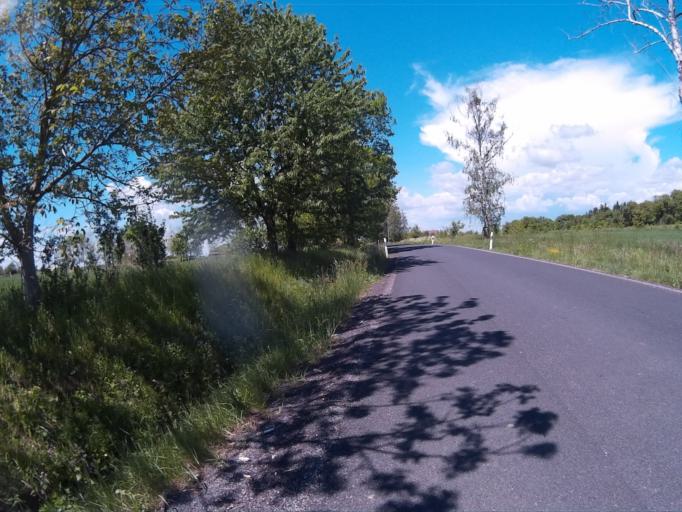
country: HU
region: Vas
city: Kormend
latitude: 46.9692
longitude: 16.5702
